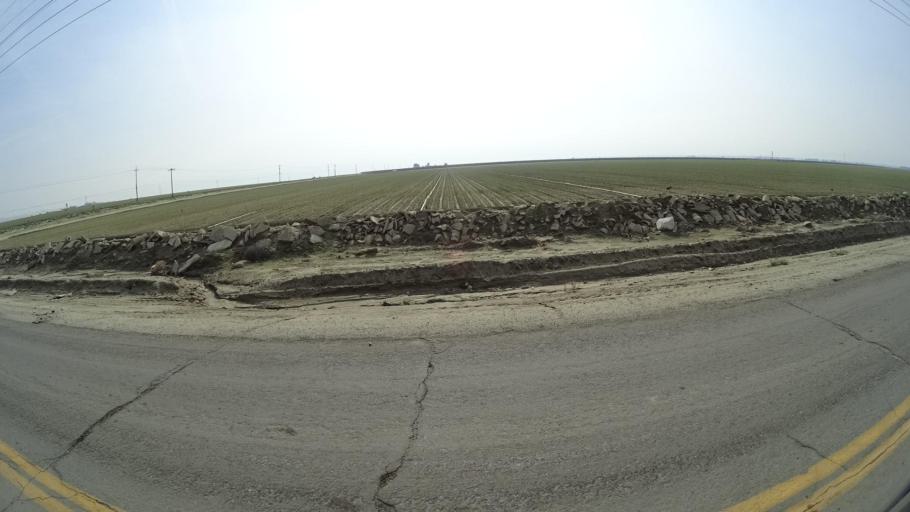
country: US
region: California
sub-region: Kern County
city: Arvin
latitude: 35.0928
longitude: -118.8474
